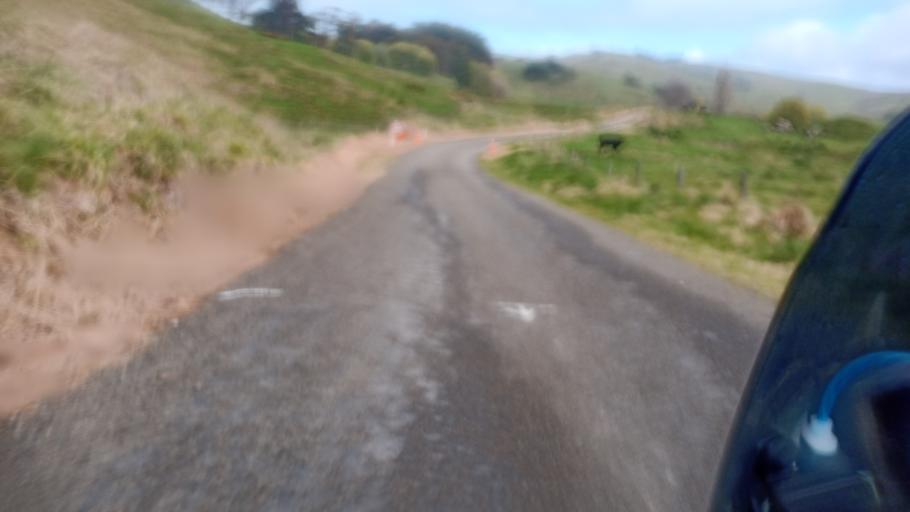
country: NZ
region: Gisborne
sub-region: Gisborne District
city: Gisborne
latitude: -38.5853
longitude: 178.1762
